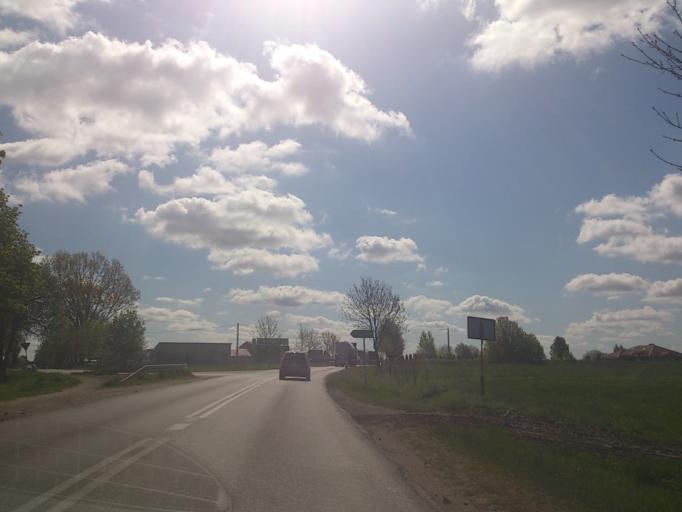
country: PL
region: Warmian-Masurian Voivodeship
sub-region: Powiat dzialdowski
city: Dzialdowo
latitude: 53.2262
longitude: 20.1991
